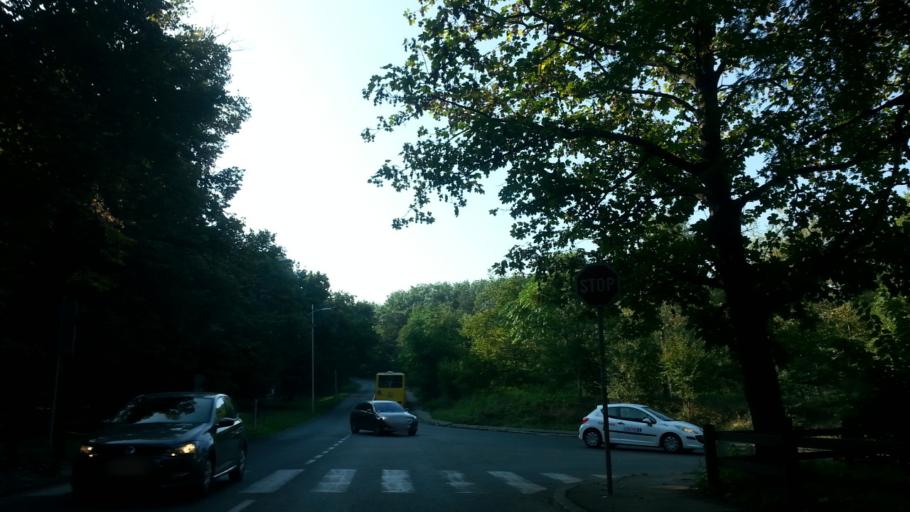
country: RS
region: Central Serbia
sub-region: Belgrade
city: Cukarica
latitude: 44.7637
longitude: 20.4299
